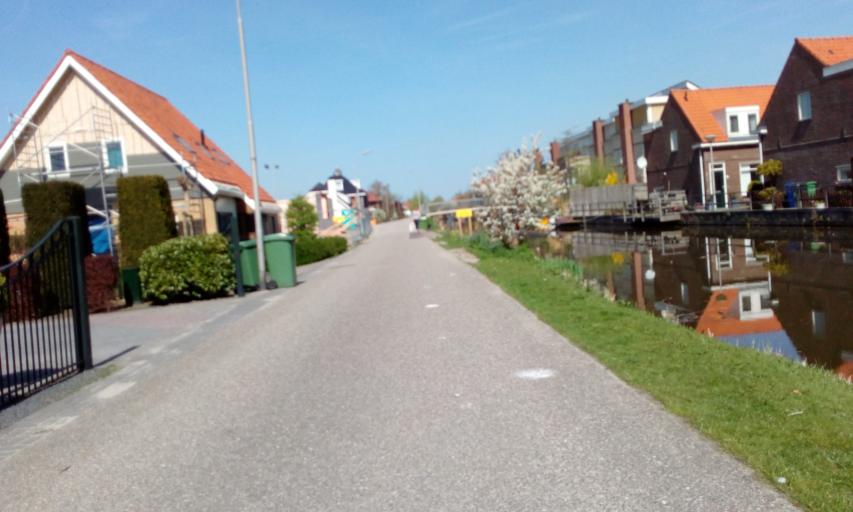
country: NL
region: South Holland
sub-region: Gemeente Delft
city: Delft
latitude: 52.0044
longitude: 4.3273
